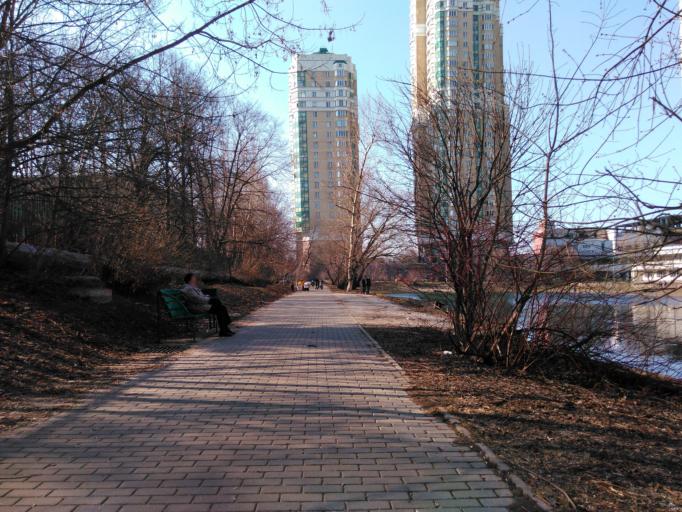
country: RU
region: Moscow
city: Ramenki
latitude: 55.6766
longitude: 37.5128
